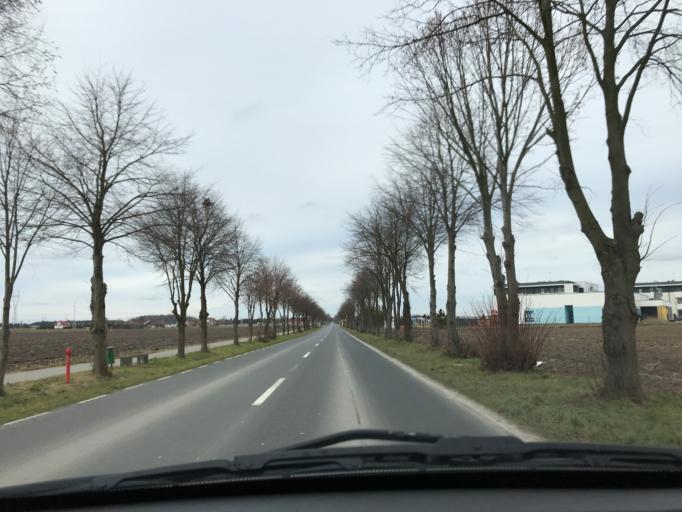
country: PL
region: Greater Poland Voivodeship
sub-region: Powiat poznanski
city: Baranowo
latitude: 52.3939
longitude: 16.7673
